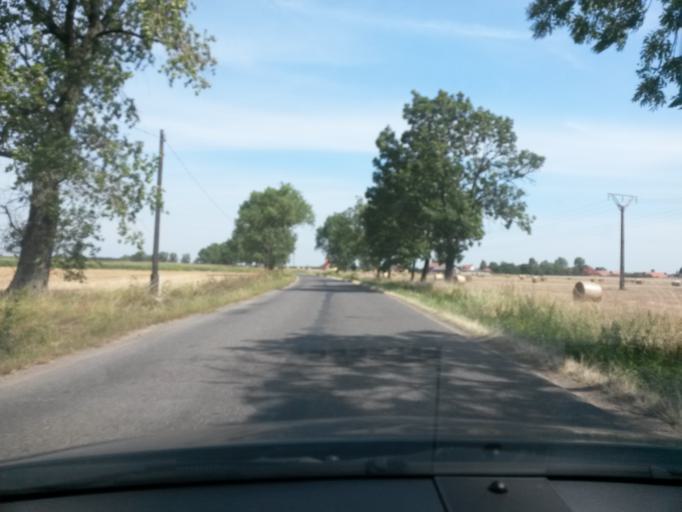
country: PL
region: Lower Silesian Voivodeship
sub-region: Powiat legnicki
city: Prochowice
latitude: 51.2210
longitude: 16.3576
